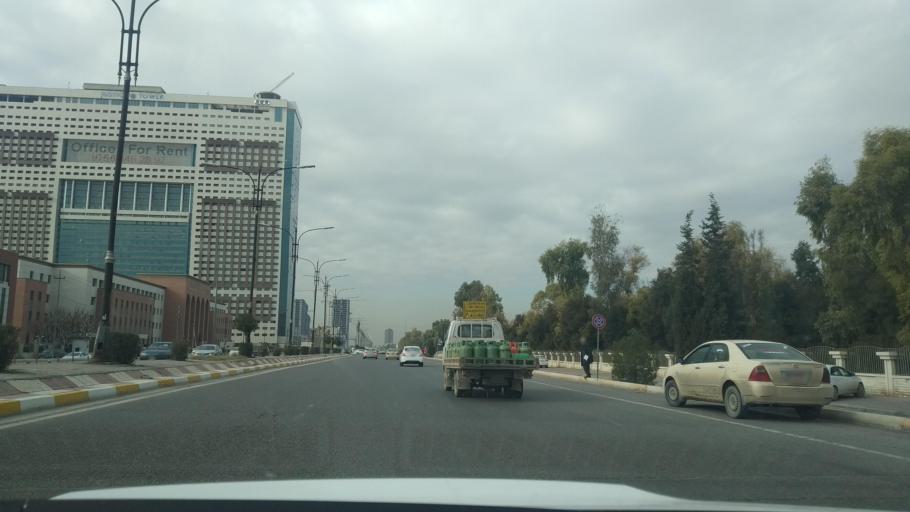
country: IQ
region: Arbil
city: Erbil
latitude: 36.1836
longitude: 43.9821
